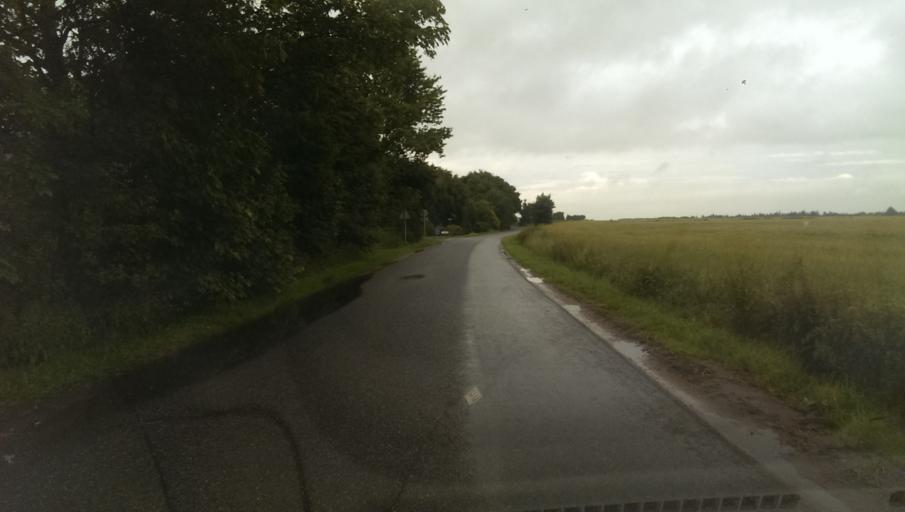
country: DK
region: South Denmark
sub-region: Esbjerg Kommune
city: Bramming
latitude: 55.4923
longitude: 8.6618
